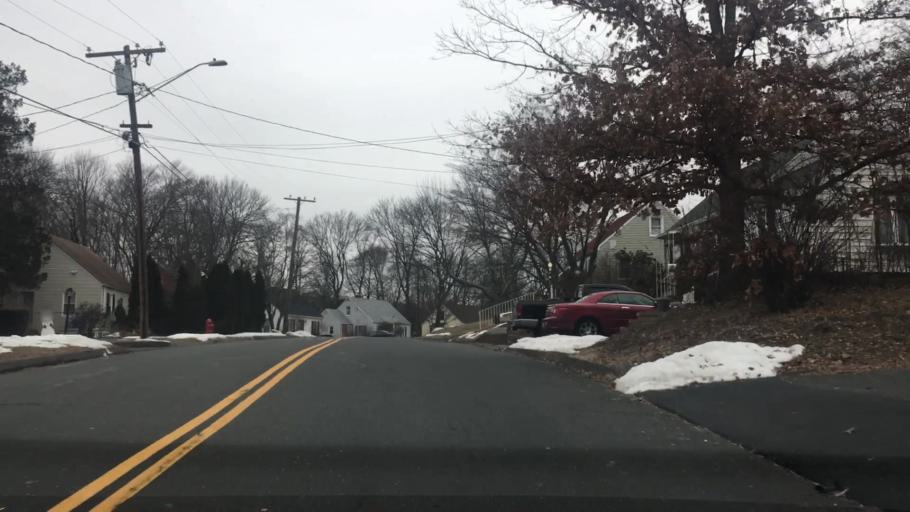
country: US
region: Connecticut
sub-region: Hartford County
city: Bristol
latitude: 41.6787
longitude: -72.9145
